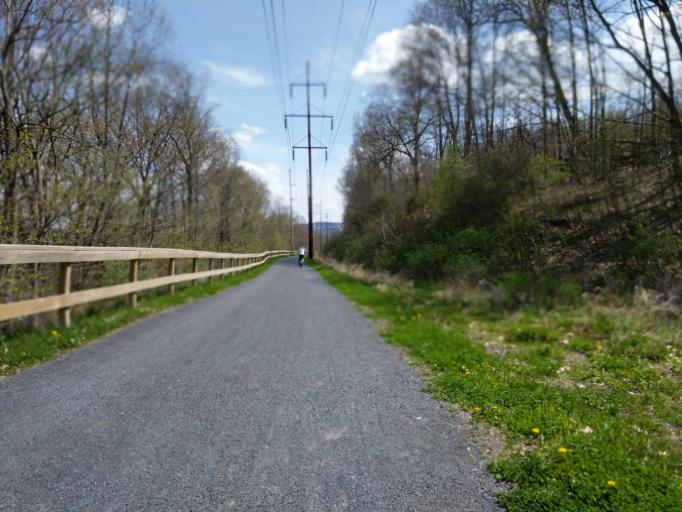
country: US
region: New York
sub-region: Tompkins County
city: Northwest Ithaca
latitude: 42.4582
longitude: -76.5205
